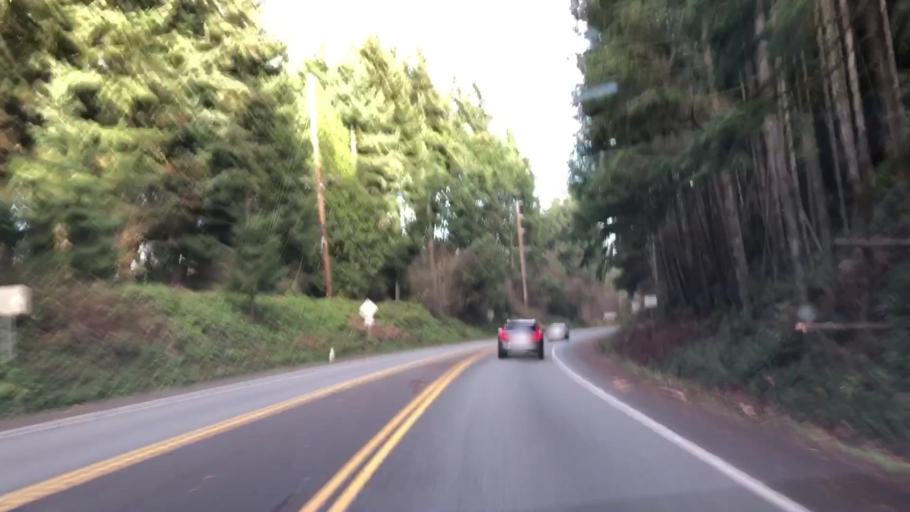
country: US
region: Washington
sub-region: Kitsap County
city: Suquamish
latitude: 47.7060
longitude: -122.5607
